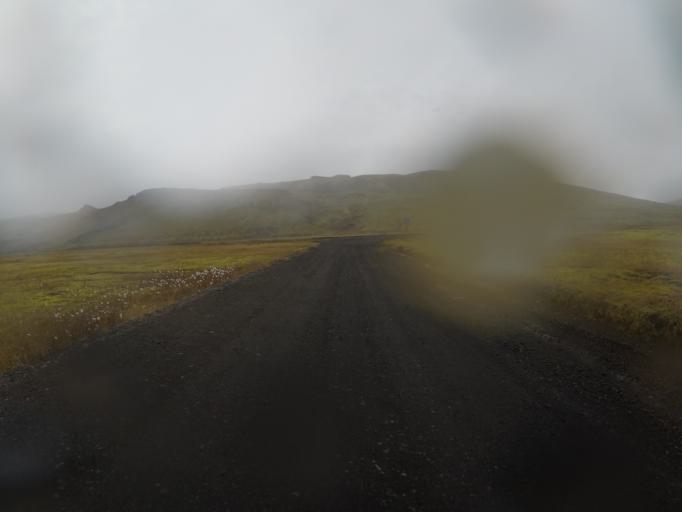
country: IS
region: South
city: Vestmannaeyjar
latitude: 63.9745
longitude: -18.8424
